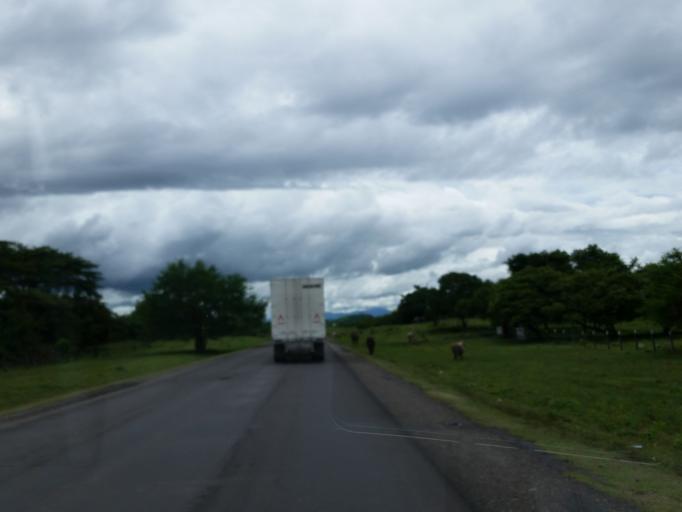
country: NI
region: Chinandega
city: Somotillo
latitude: 12.8933
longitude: -86.8506
